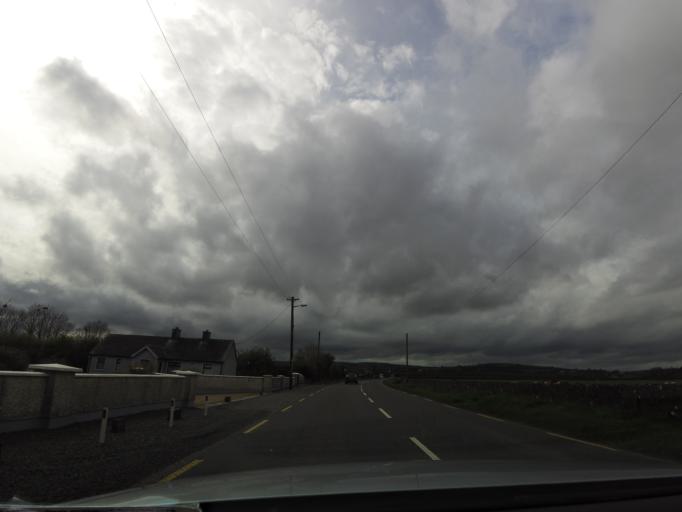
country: IE
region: Leinster
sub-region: Kilkenny
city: Ballyragget
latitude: 52.7349
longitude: -7.4099
